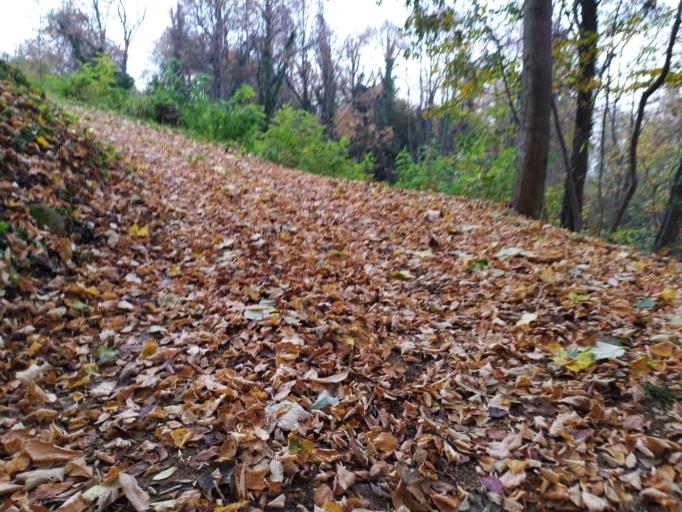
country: IT
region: Veneto
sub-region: Provincia di Vicenza
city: Schio
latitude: 45.6909
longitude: 11.3562
